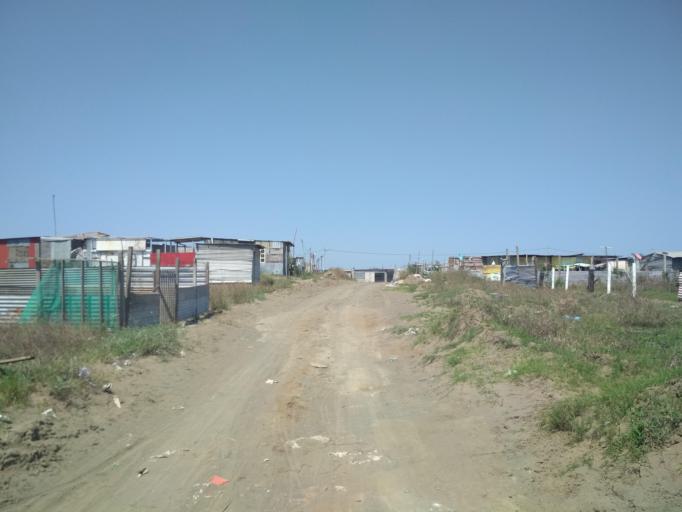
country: MX
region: Veracruz
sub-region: Veracruz
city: Lomas de Rio Medio Cuatro
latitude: 19.1875
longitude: -96.1961
